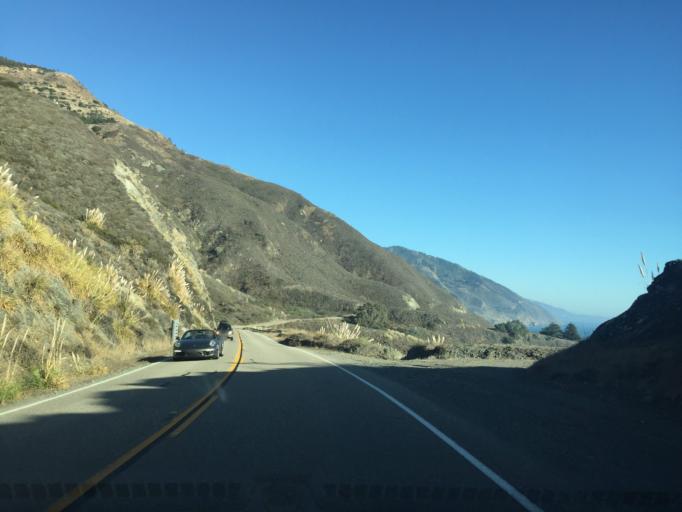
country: US
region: California
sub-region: Monterey County
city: King City
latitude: 35.8718
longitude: -121.4433
